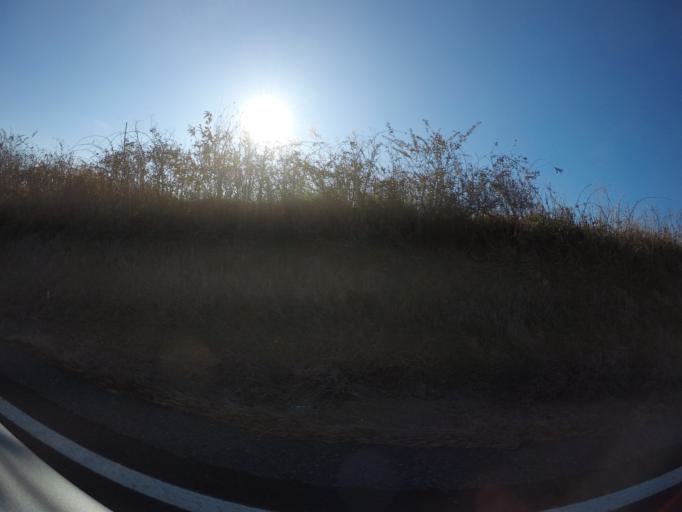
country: US
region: Maryland
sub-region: Harford County
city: South Bel Air
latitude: 39.6214
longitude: -76.2590
